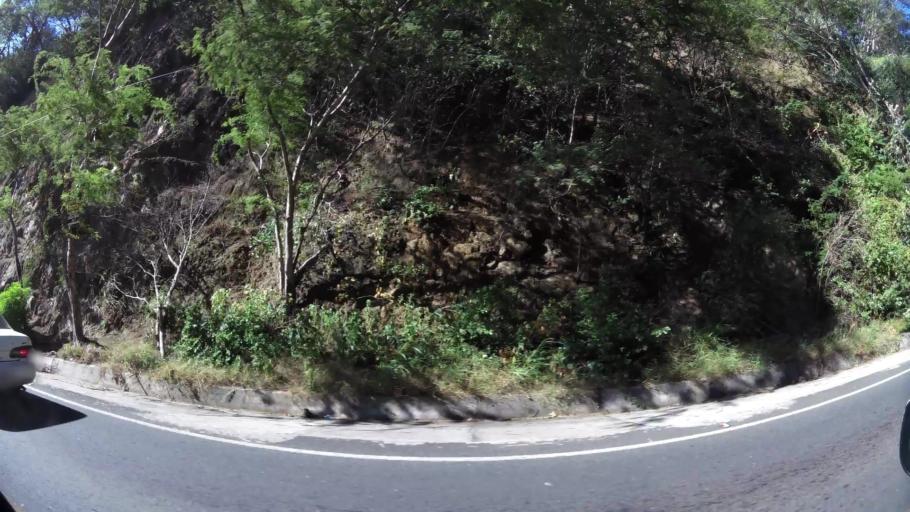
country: CR
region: Guanacaste
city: Belen
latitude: 10.3657
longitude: -85.7571
